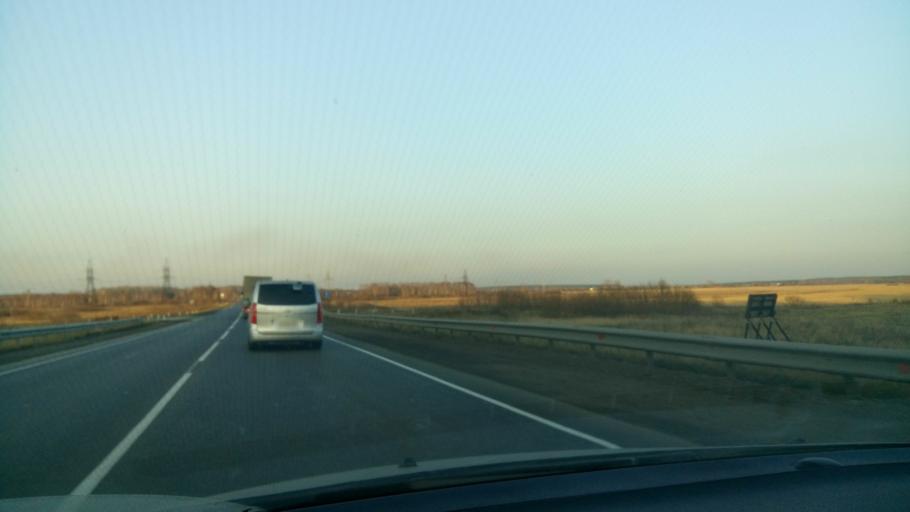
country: RU
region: Sverdlovsk
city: Yelanskiy
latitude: 56.7999
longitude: 62.5177
